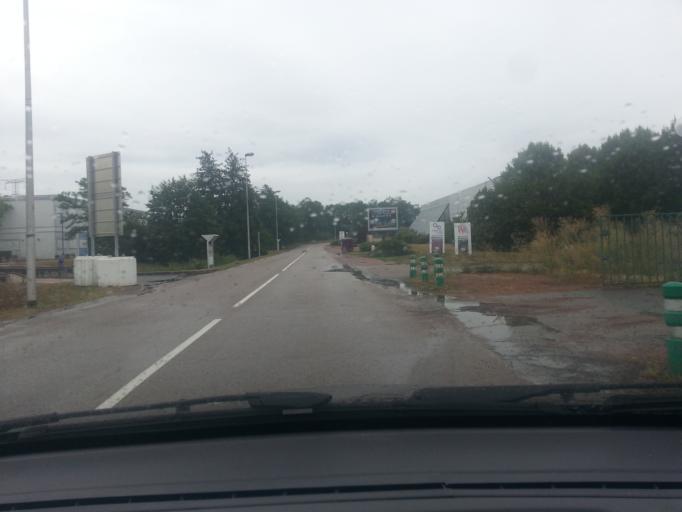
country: FR
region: Bourgogne
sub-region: Departement de Saone-et-Loire
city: Montchanin
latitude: 46.7637
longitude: 4.4983
